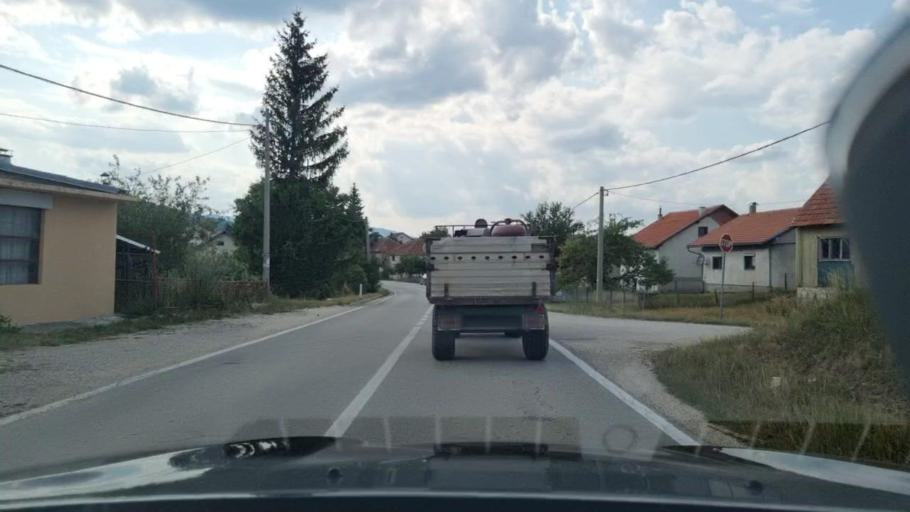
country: BA
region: Federation of Bosnia and Herzegovina
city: Glamoc
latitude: 44.0457
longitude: 16.8624
